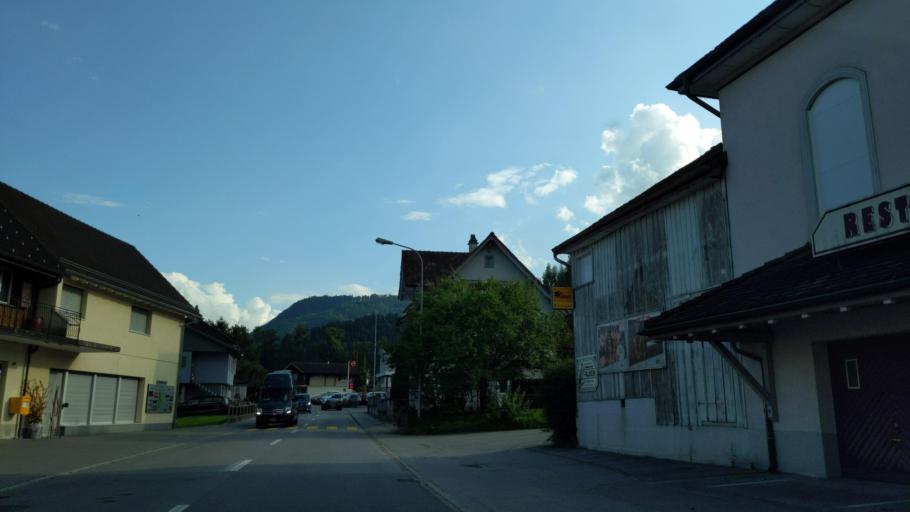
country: CH
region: Saint Gallen
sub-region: Wahlkreis Rheintal
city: Eichberg
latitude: 47.3414
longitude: 9.5309
